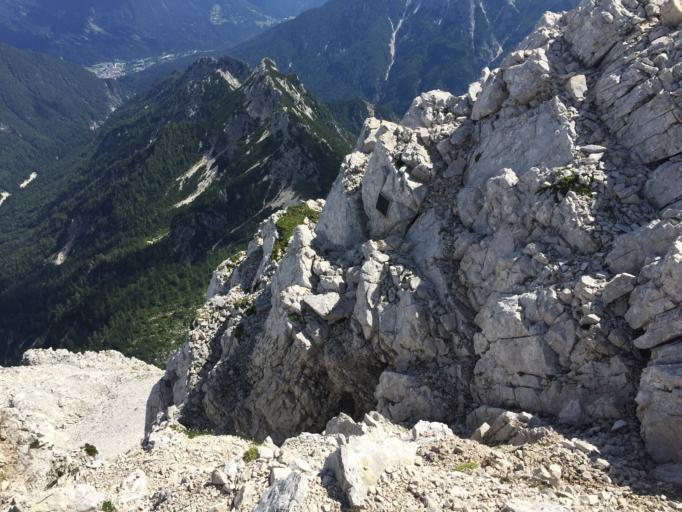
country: SI
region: Kranjska Gora
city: Kranjska Gora
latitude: 46.4376
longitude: 13.7309
